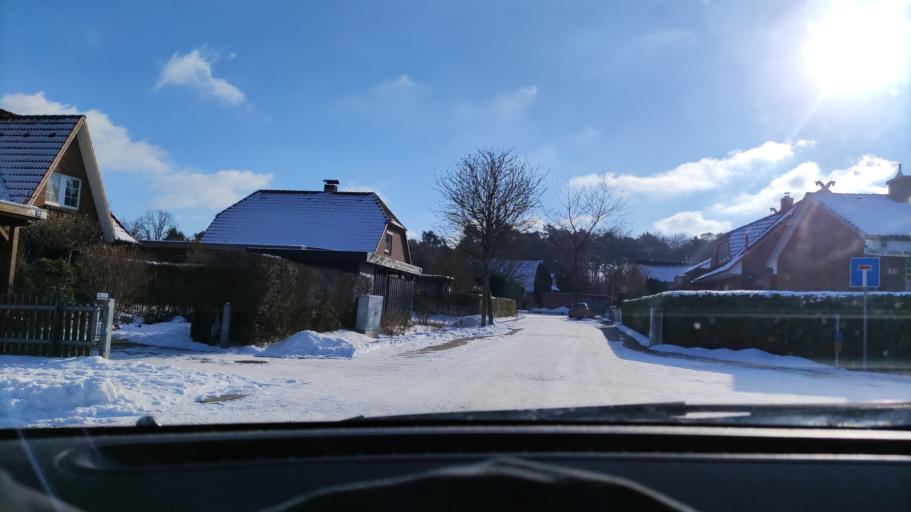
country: DE
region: Lower Saxony
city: Wendisch Evern
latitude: 53.2167
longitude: 10.4785
